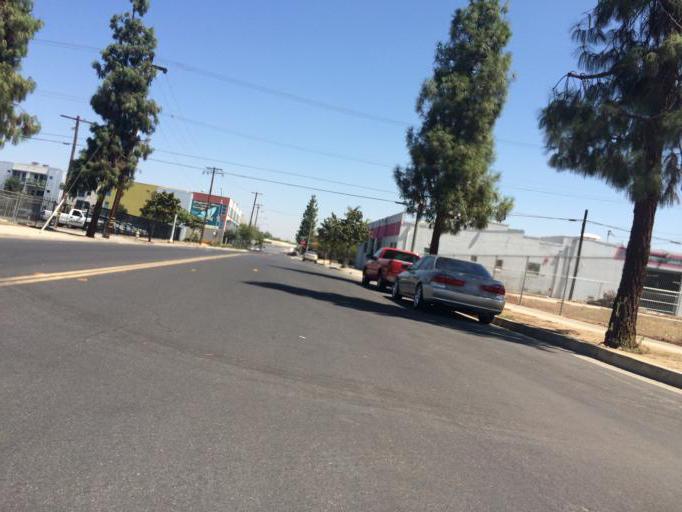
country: US
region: California
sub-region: Fresno County
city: Fresno
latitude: 36.7415
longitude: -119.8019
